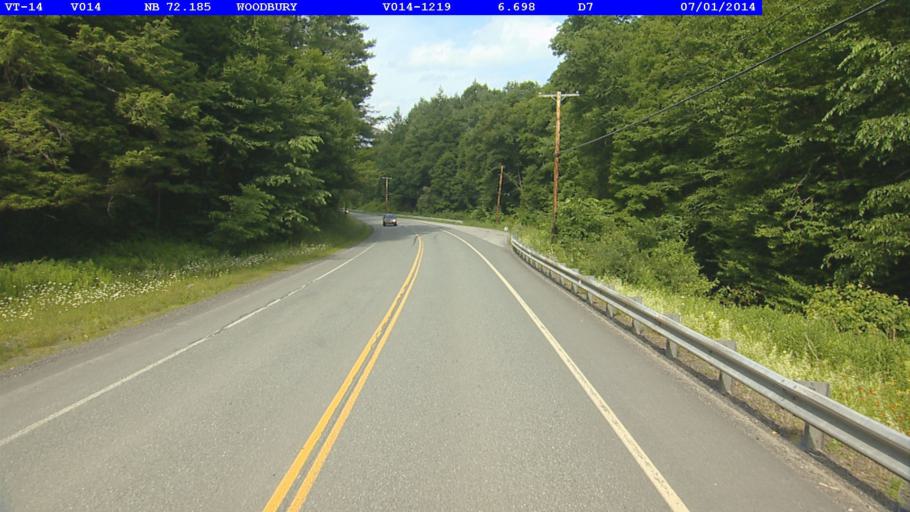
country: US
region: Vermont
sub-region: Caledonia County
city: Hardwick
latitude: 44.4753
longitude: -72.3945
